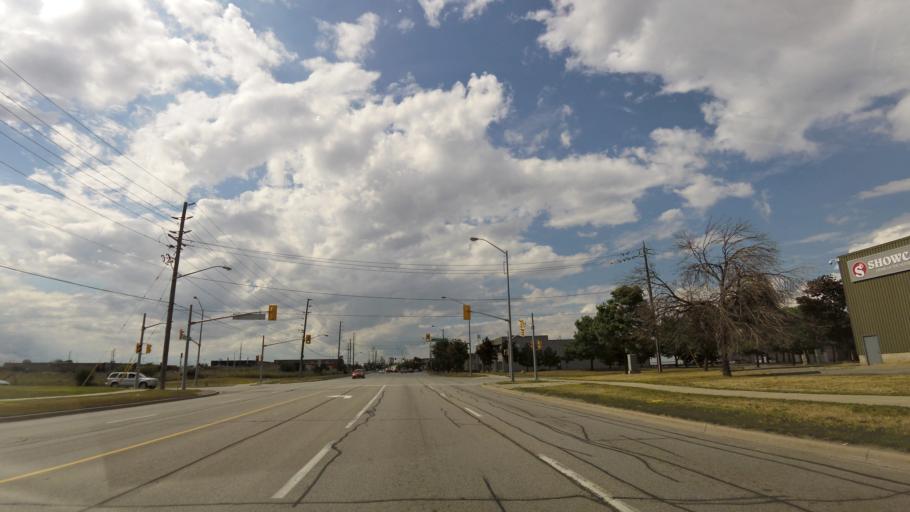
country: CA
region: Ontario
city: Brampton
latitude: 43.6887
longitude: -79.7042
